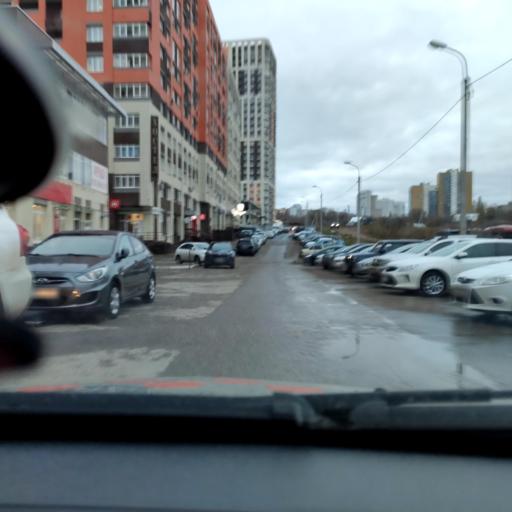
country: RU
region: Bashkortostan
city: Ufa
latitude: 54.7177
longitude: 55.9796
